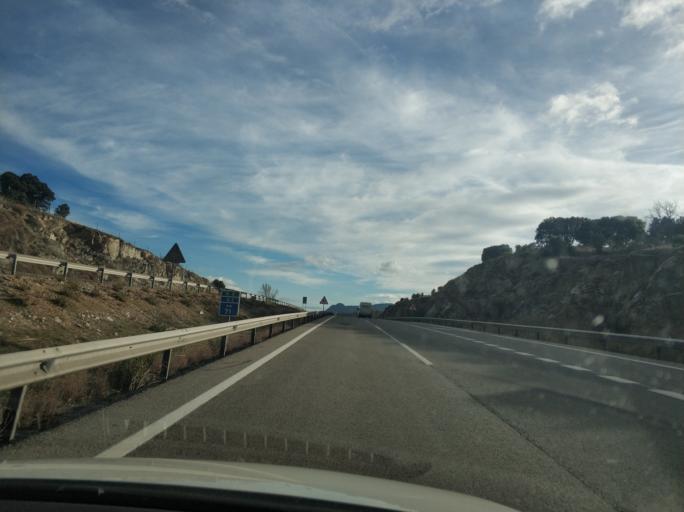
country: ES
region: Madrid
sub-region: Provincia de Madrid
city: Buitrago del Lozoya
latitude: 40.9562
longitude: -3.6413
